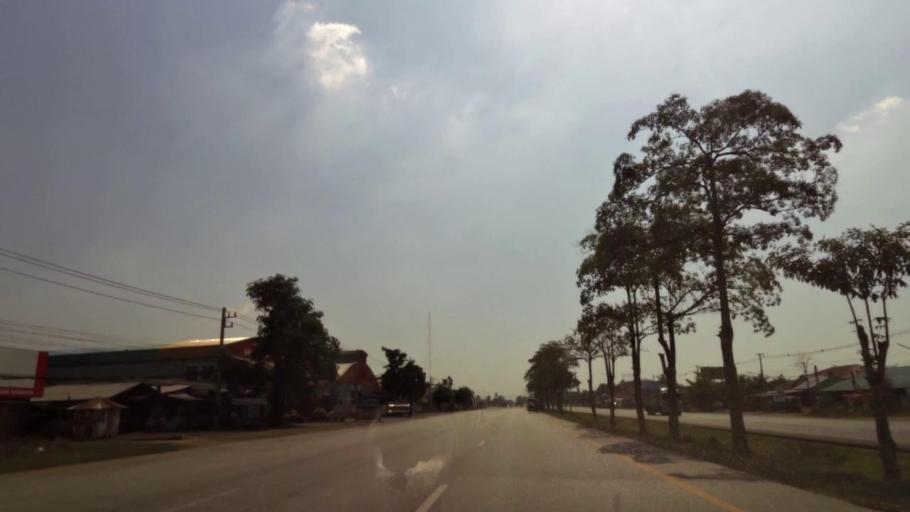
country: TH
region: Phichit
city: Bueng Na Rang
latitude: 16.1280
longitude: 100.1256
